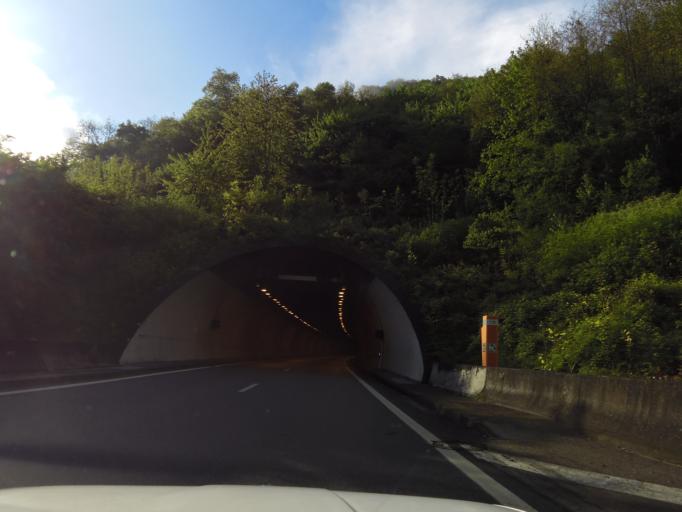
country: FR
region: Rhone-Alpes
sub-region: Departement de la Savoie
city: Aiton
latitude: 45.5395
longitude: 6.3033
